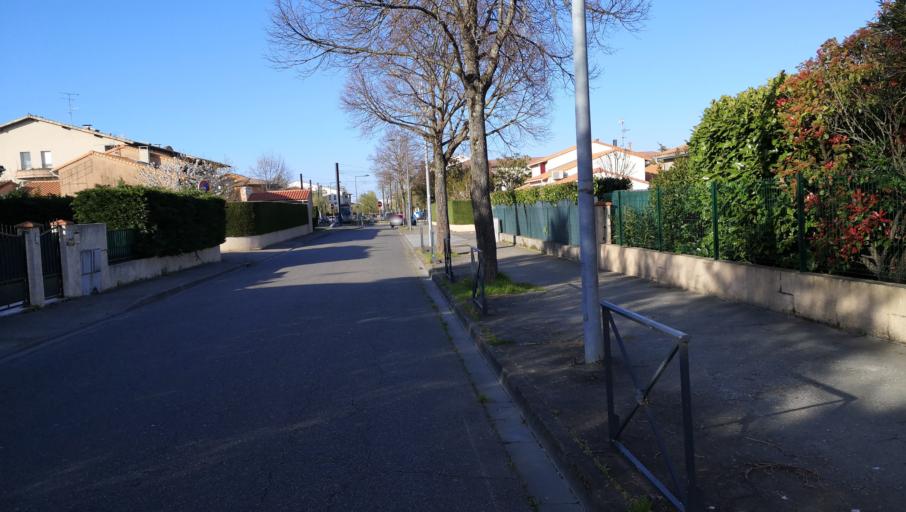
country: FR
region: Midi-Pyrenees
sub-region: Departement de la Haute-Garonne
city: Blagnac
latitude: 43.6443
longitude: 1.3759
